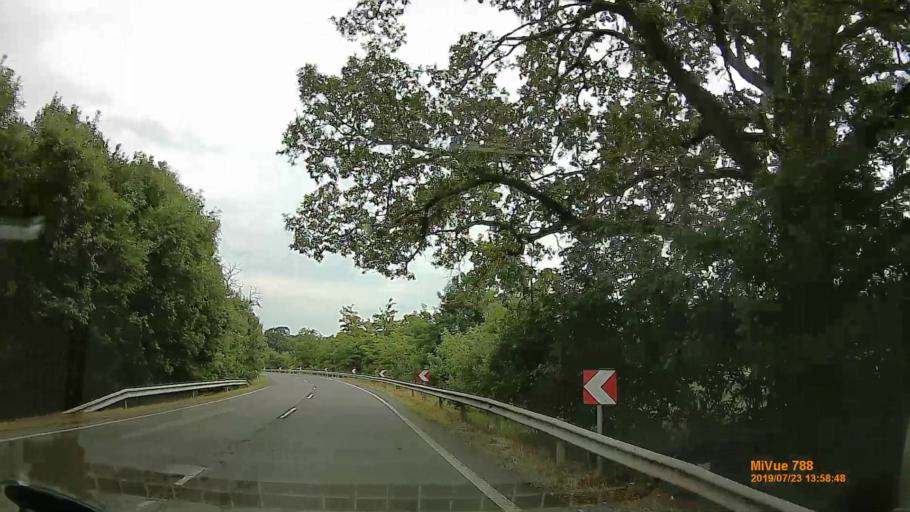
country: HU
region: Szabolcs-Szatmar-Bereg
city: Tiszavasvari
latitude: 47.9262
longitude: 21.2813
